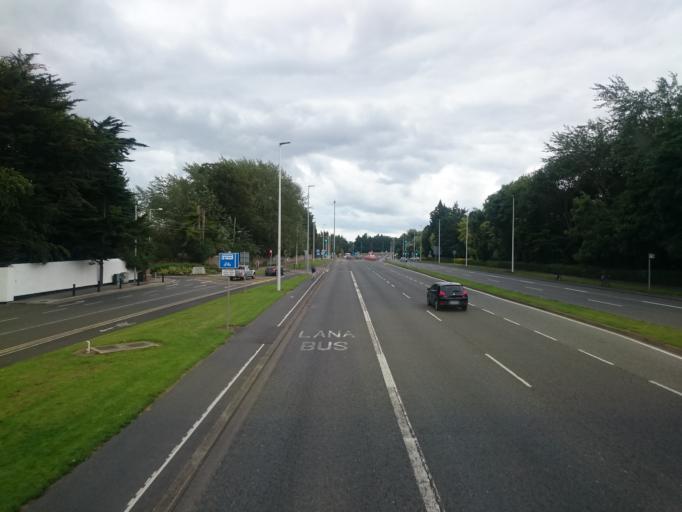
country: IE
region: Leinster
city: Mount Merrion
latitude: 53.3052
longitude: -6.2106
